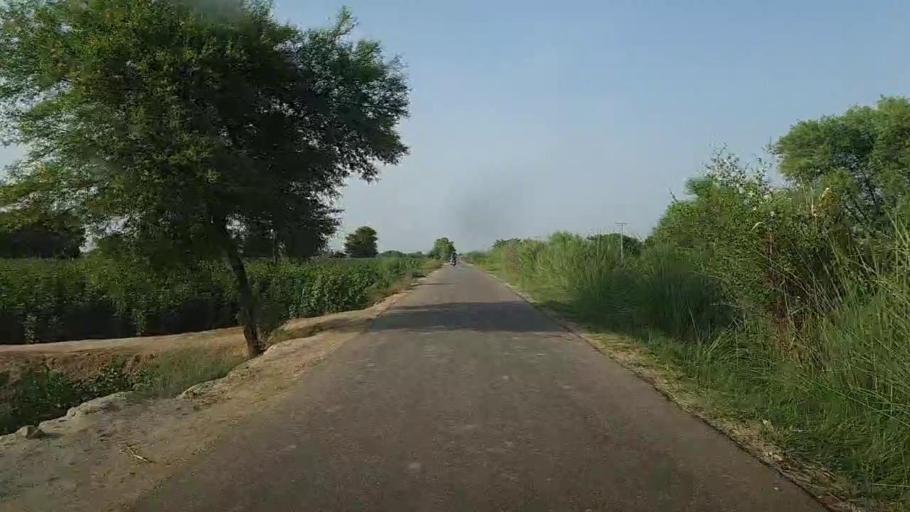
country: PK
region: Sindh
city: Khairpur
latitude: 28.0769
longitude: 69.8122
